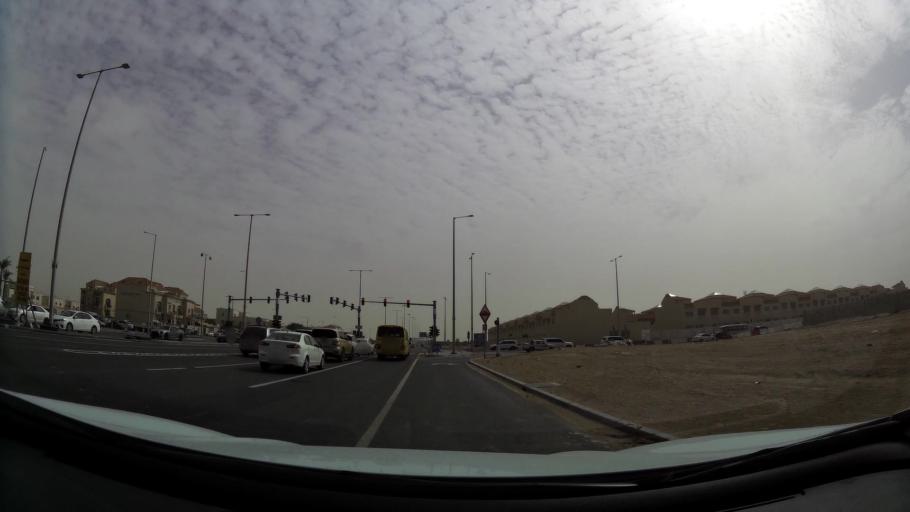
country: AE
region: Abu Dhabi
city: Abu Dhabi
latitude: 24.4042
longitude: 54.5718
